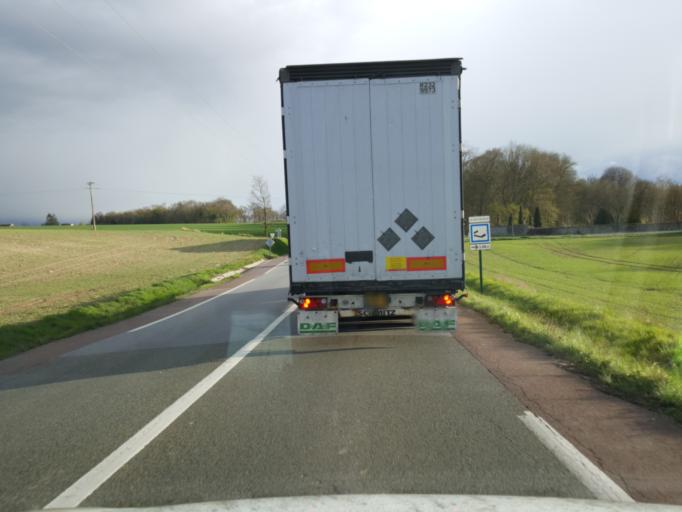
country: FR
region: Ile-de-France
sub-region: Departement des Yvelines
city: Follainville-Dennemont
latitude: 49.0348
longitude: 1.7485
